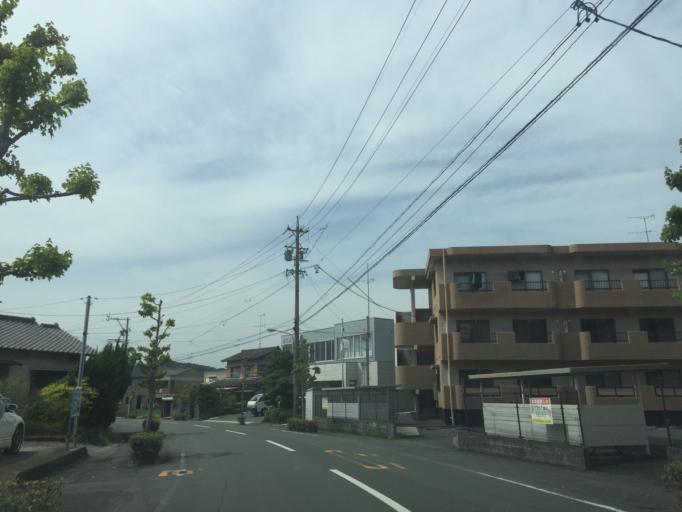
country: JP
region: Shizuoka
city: Kakegawa
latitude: 34.7820
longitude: 138.0161
